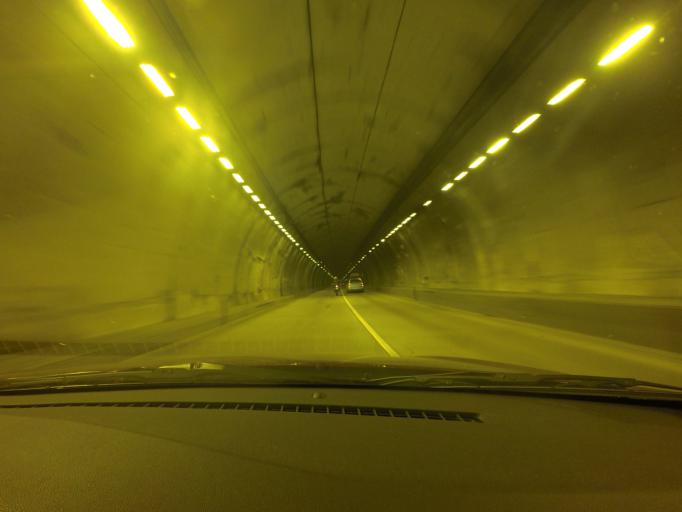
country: CO
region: Cundinamarca
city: Nilo
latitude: 4.2663
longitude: -74.5866
